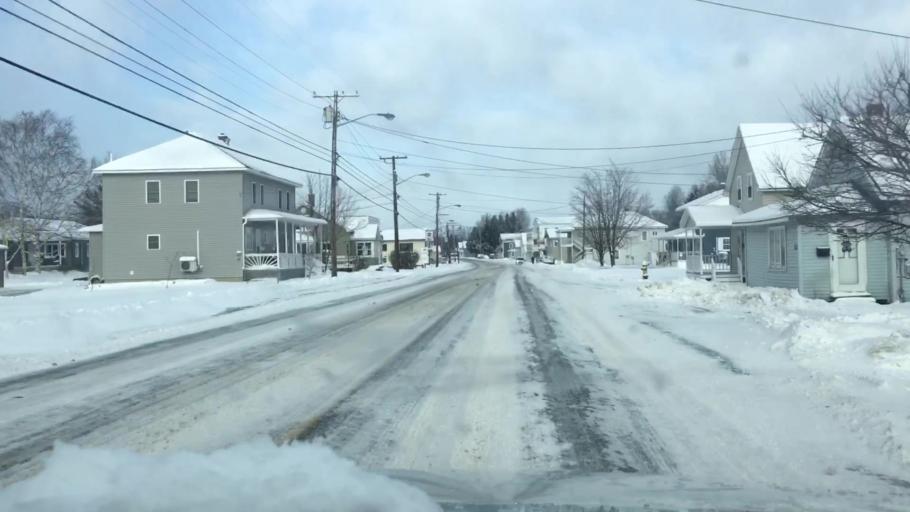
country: US
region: Maine
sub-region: Aroostook County
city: Van Buren
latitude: 47.1849
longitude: -67.9554
